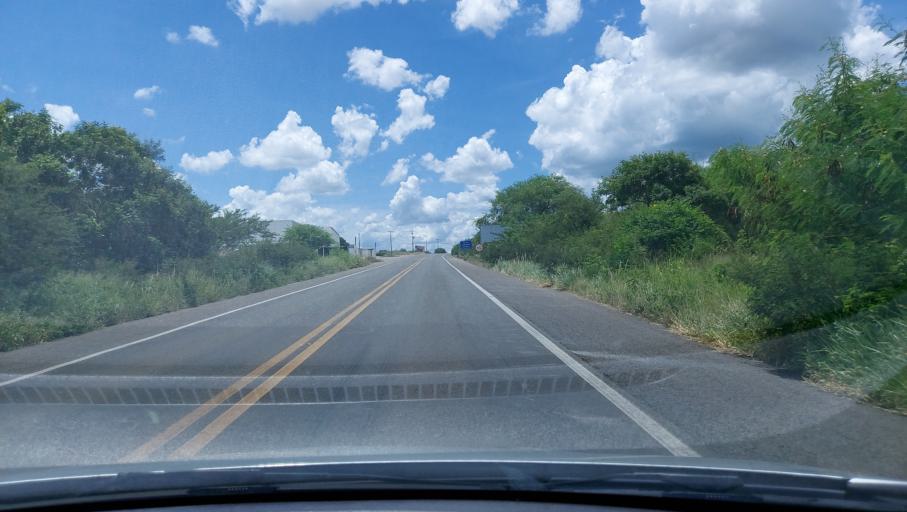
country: BR
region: Bahia
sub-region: Itaberaba
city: Itaberaba
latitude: -12.5211
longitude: -40.2742
